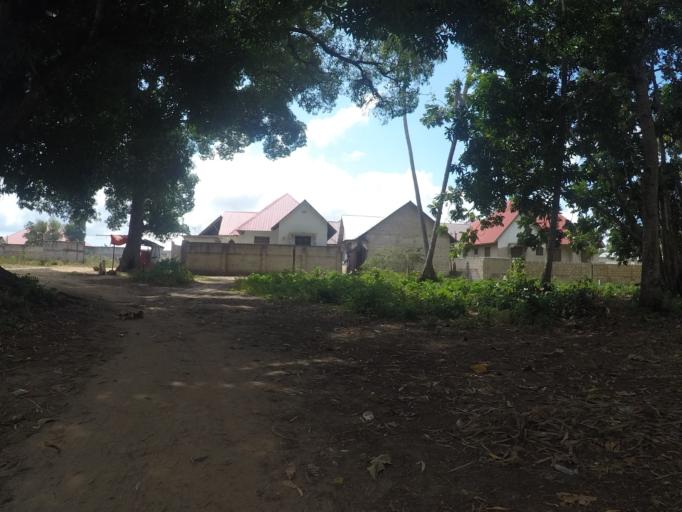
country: TZ
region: Zanzibar Urban/West
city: Zanzibar
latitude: -6.2015
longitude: 39.2348
